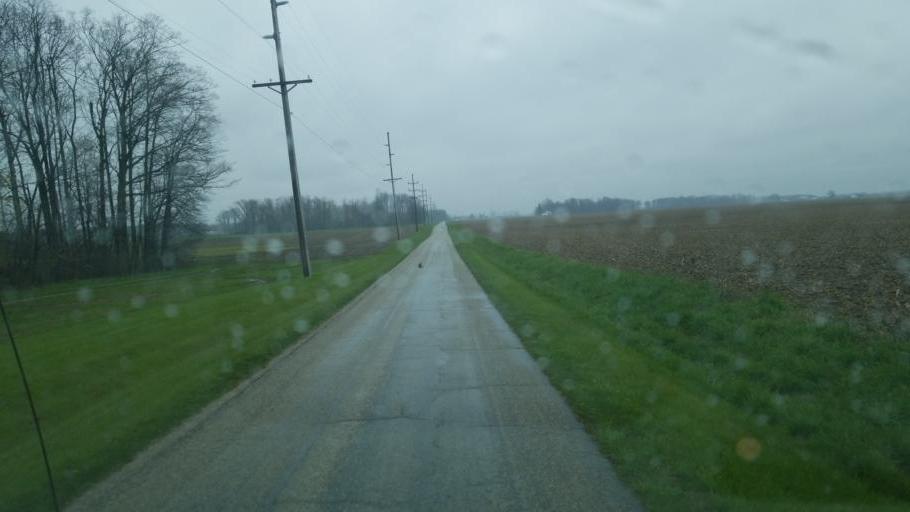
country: US
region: Ohio
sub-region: Crawford County
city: Bucyrus
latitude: 40.8338
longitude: -83.0873
